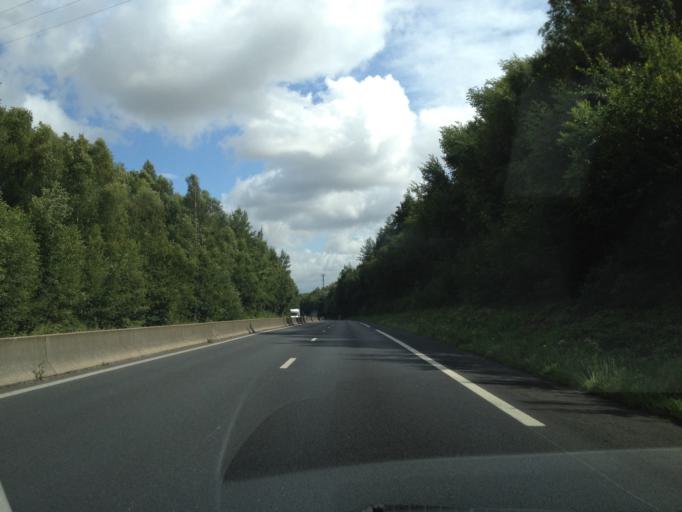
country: FR
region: Haute-Normandie
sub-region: Departement de la Seine-Maritime
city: Quincampoix
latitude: 49.5107
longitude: 1.1863
